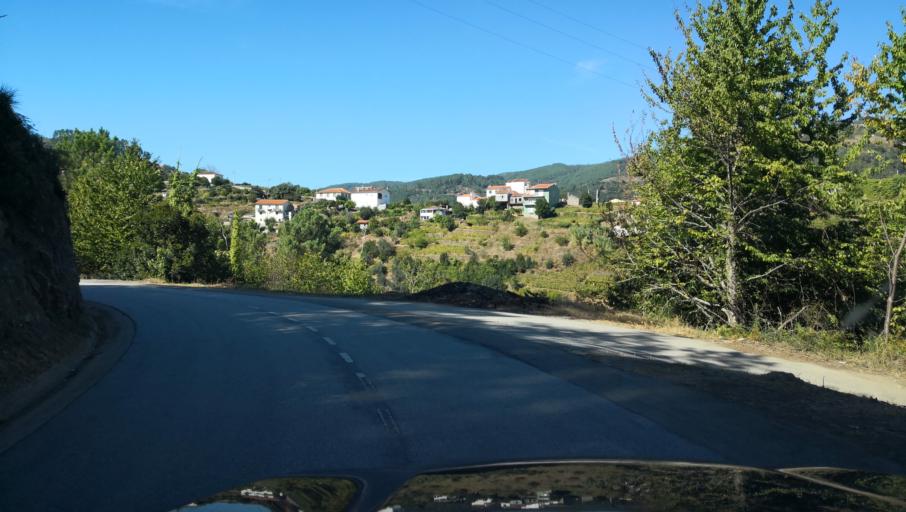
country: PT
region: Vila Real
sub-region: Santa Marta de Penaguiao
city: Santa Marta de Penaguiao
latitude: 41.2438
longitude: -7.8097
